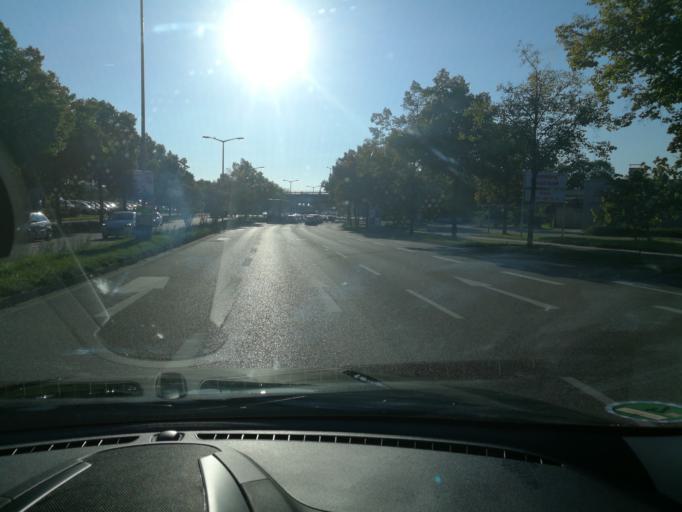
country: DE
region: Bavaria
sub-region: Upper Palatinate
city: Regensburg
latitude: 49.0138
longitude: 12.1449
